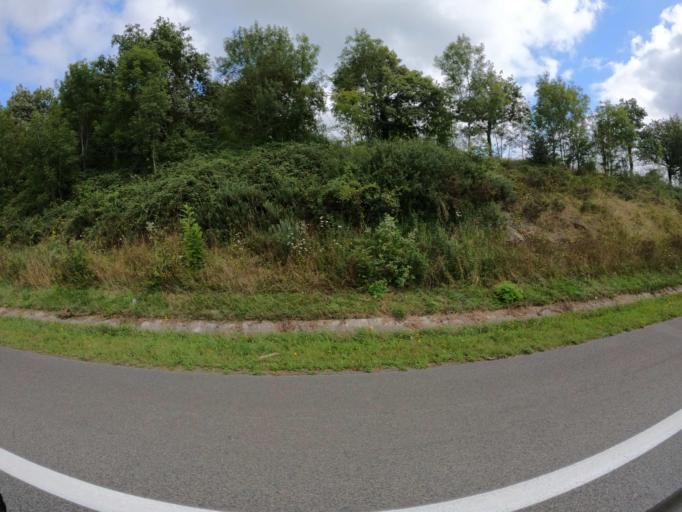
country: FR
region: Limousin
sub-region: Departement de la Haute-Vienne
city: Saint-Victurnien
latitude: 45.8902
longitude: 1.0536
